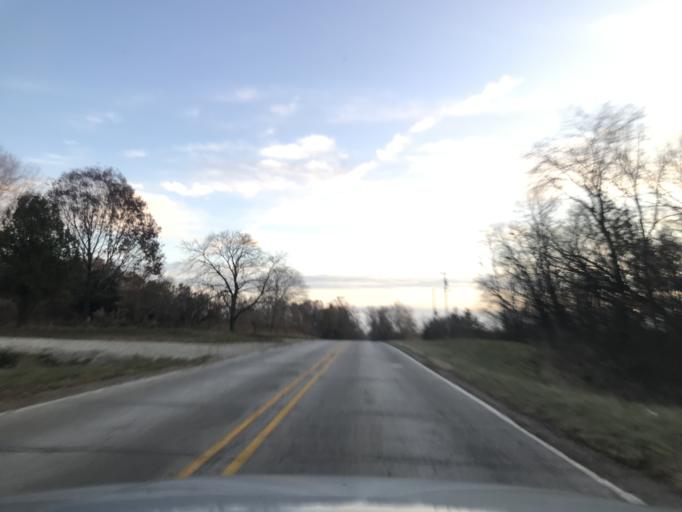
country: US
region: Illinois
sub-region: Henderson County
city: Oquawka
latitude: 40.9141
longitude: -90.8643
